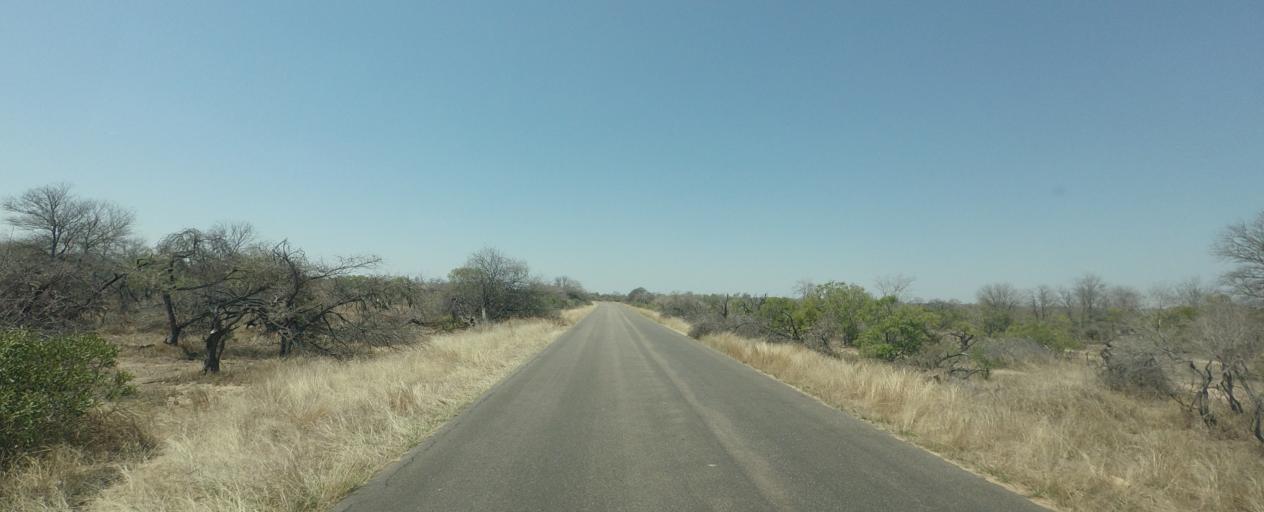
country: ZA
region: Limpopo
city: Thulamahashi
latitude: -24.4361
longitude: 31.4945
